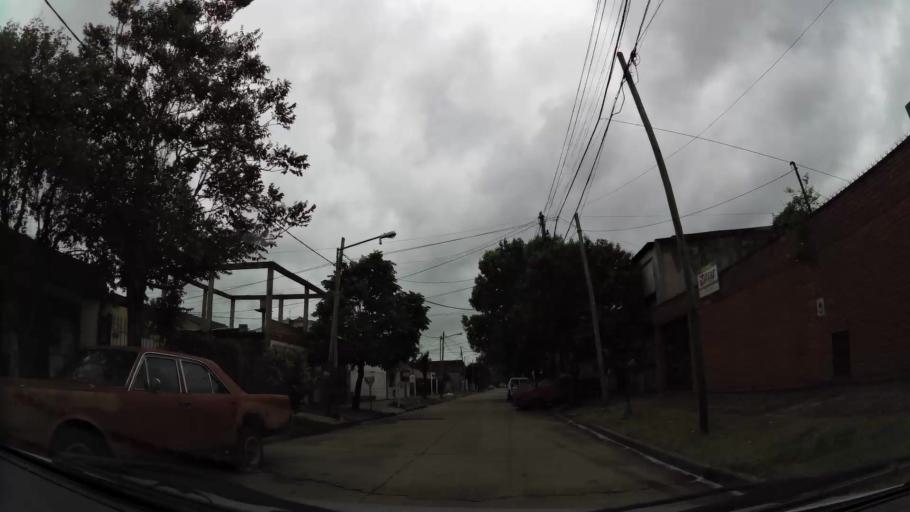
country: AR
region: Buenos Aires
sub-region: Partido de Lomas de Zamora
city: Lomas de Zamora
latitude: -34.7526
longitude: -58.3719
